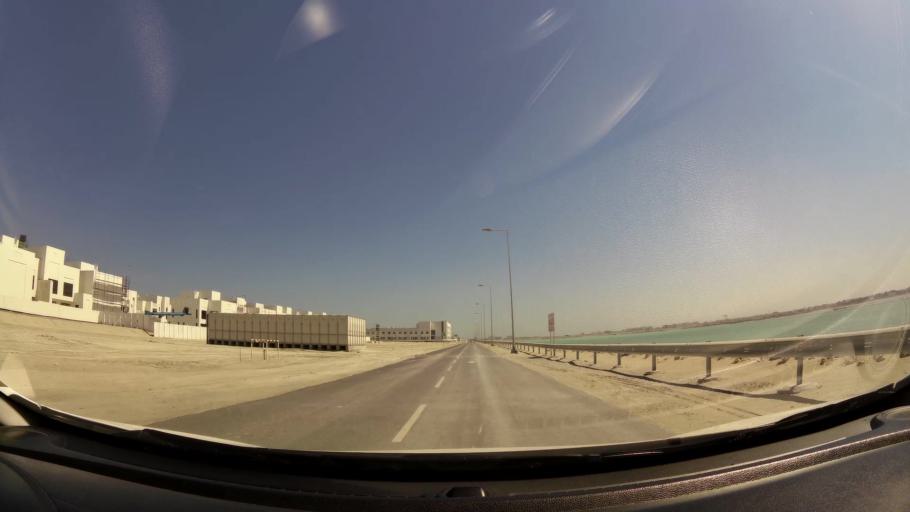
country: BH
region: Muharraq
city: Al Muharraq
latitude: 26.2998
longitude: 50.6328
